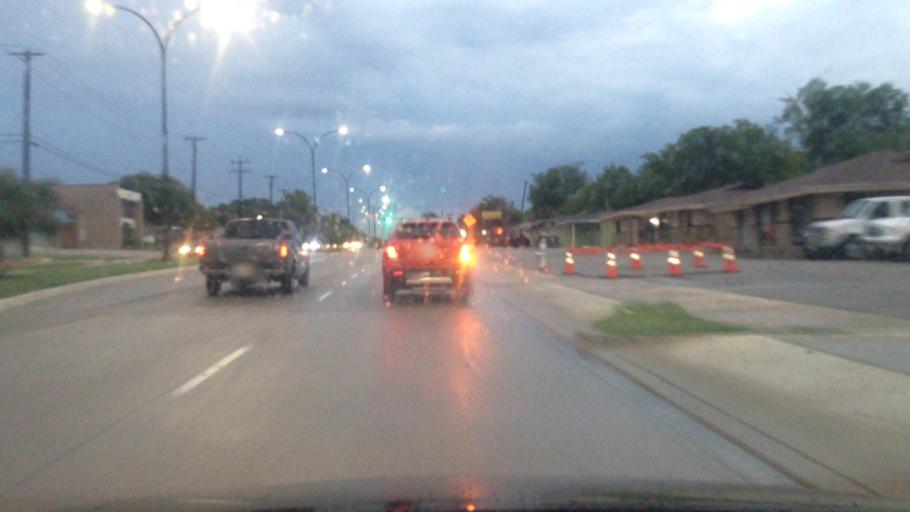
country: US
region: Texas
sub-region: Tarrant County
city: Arlington
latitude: 32.7353
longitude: -97.0821
